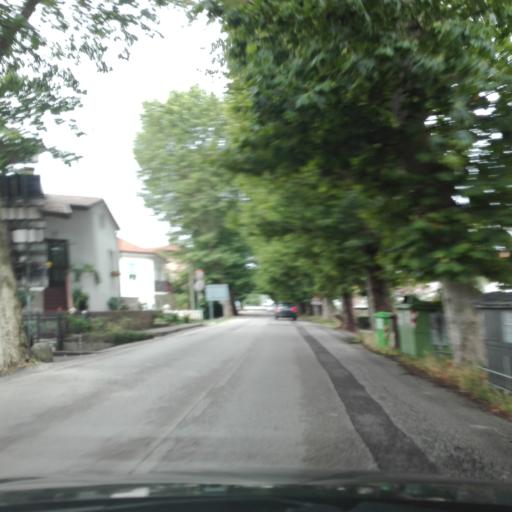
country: IT
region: Veneto
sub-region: Provincia di Rovigo
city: Rovigo
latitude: 45.0742
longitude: 11.7765
